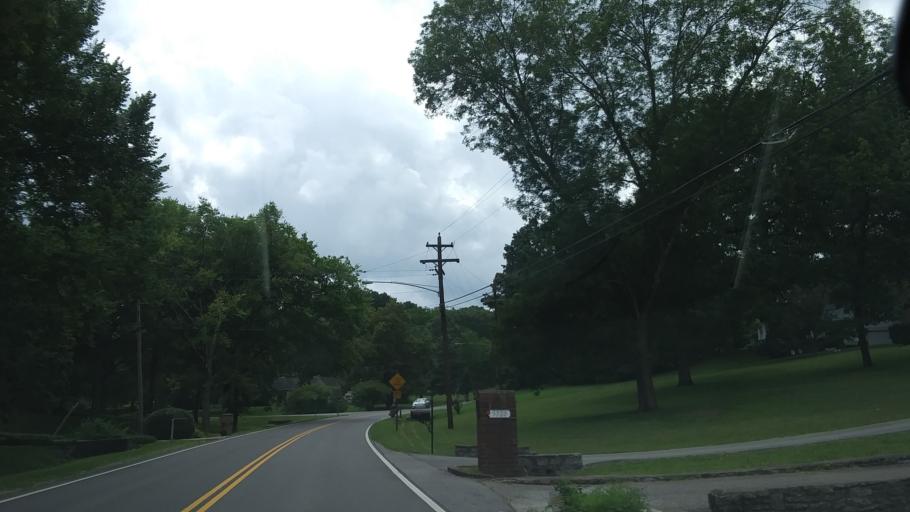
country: US
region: Tennessee
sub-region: Davidson County
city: Belle Meade
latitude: 36.1379
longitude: -86.8682
